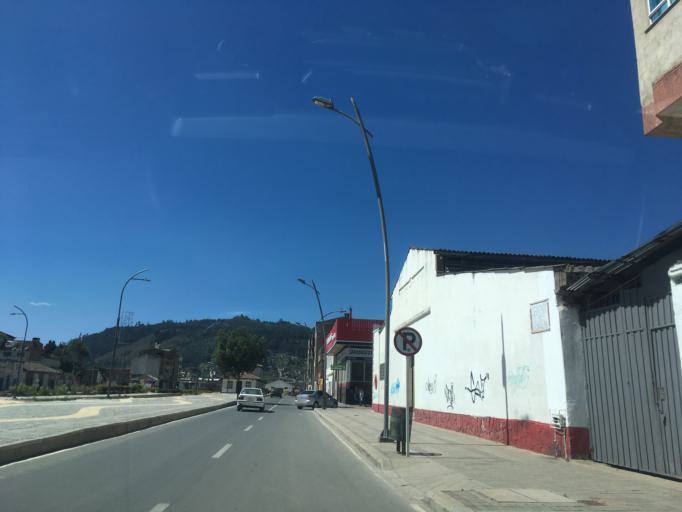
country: CO
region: Boyaca
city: Duitama
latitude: 5.8249
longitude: -73.0311
